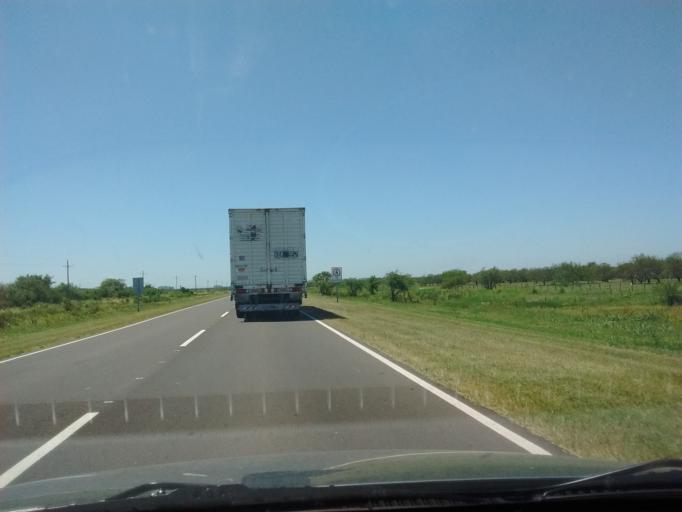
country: AR
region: Entre Rios
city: General Galarza
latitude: -32.8907
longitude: -59.6928
